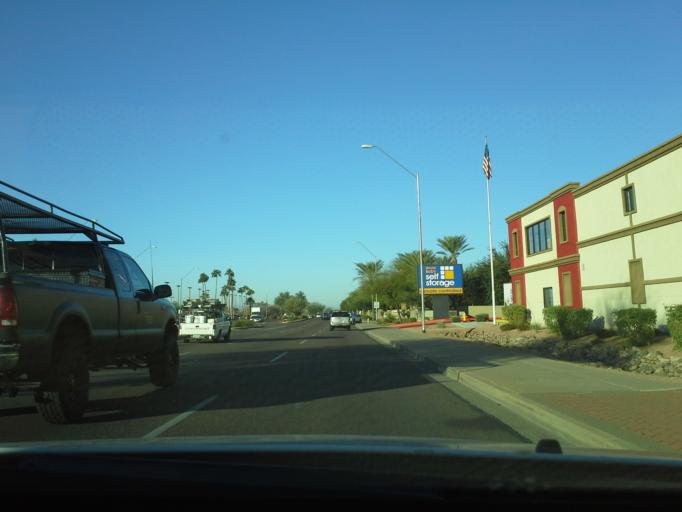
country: US
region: Arizona
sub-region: Maricopa County
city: Paradise Valley
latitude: 33.6407
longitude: -112.0398
